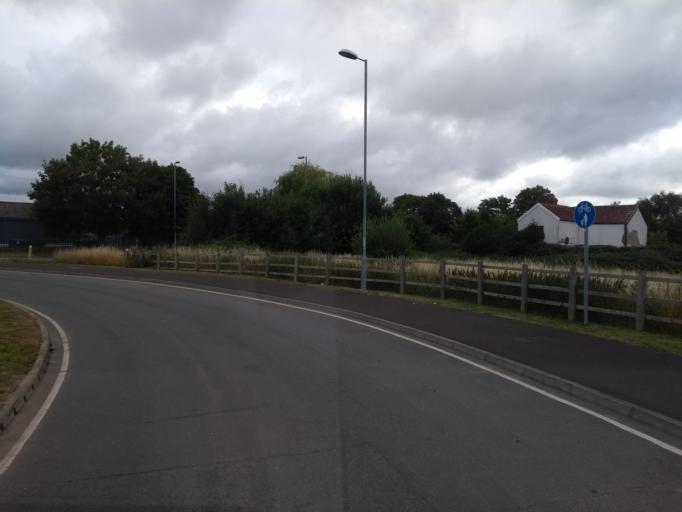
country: GB
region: England
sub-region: Somerset
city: Ilminster
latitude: 50.9328
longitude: -2.9344
